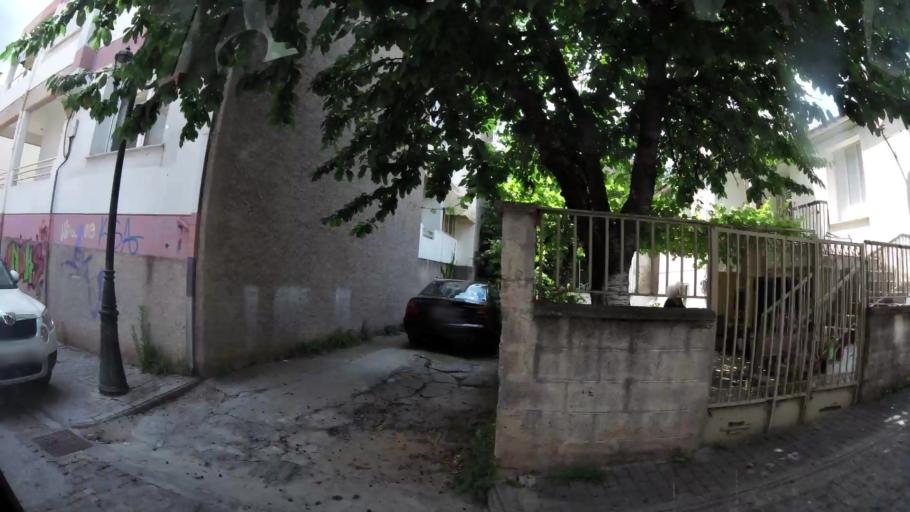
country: GR
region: West Macedonia
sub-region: Nomos Kozanis
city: Kozani
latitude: 40.3055
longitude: 21.7921
